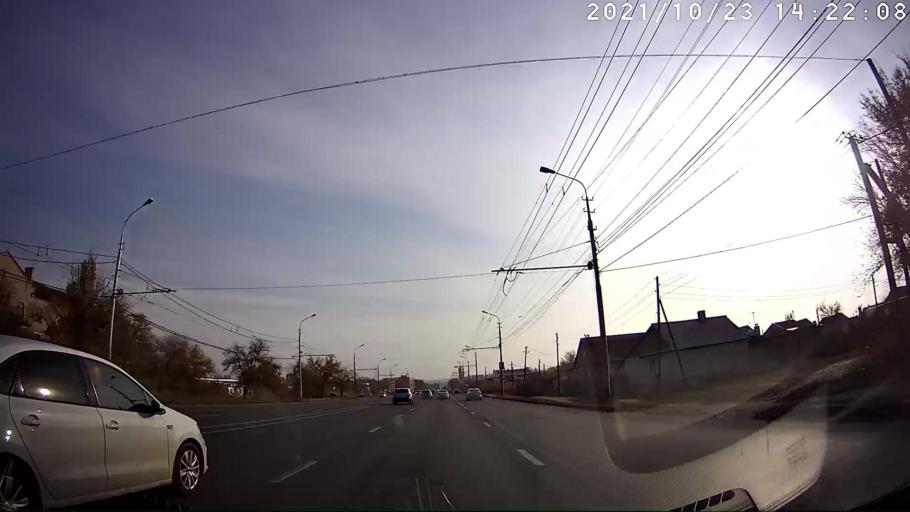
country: RU
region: Volgograd
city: Volgograd
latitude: 48.5877
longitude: 44.4211
